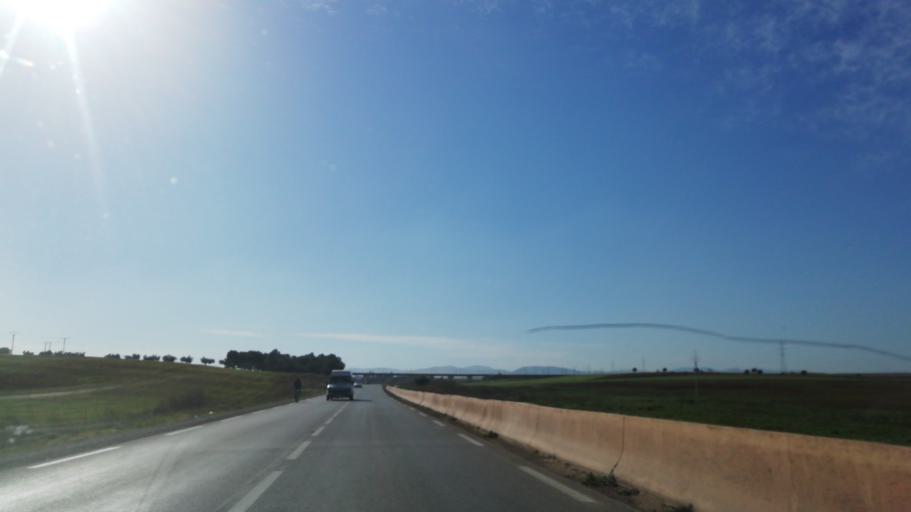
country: DZ
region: Tlemcen
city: Ouled Mimoun
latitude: 35.0154
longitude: -0.9050
